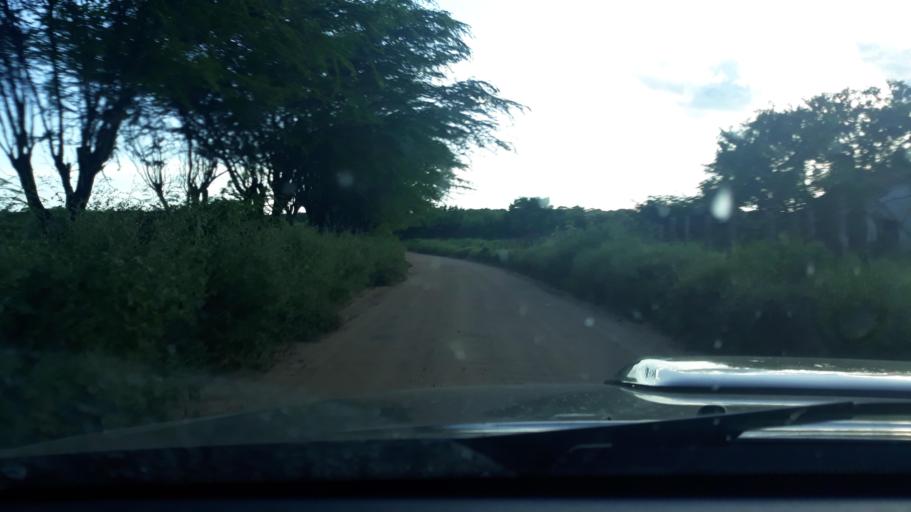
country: BR
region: Bahia
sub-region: Riacho De Santana
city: Riacho de Santana
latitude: -13.8103
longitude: -42.7191
